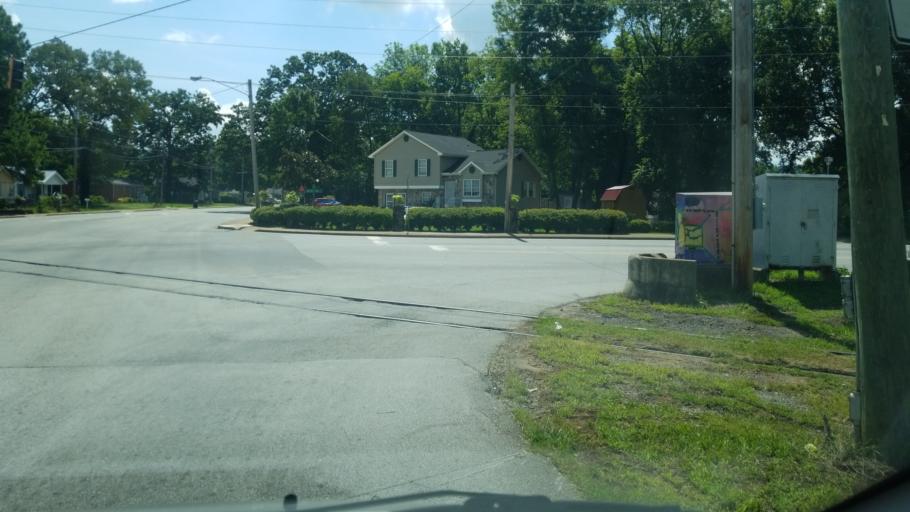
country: US
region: Tennessee
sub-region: Hamilton County
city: East Chattanooga
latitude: 35.0555
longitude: -85.2694
